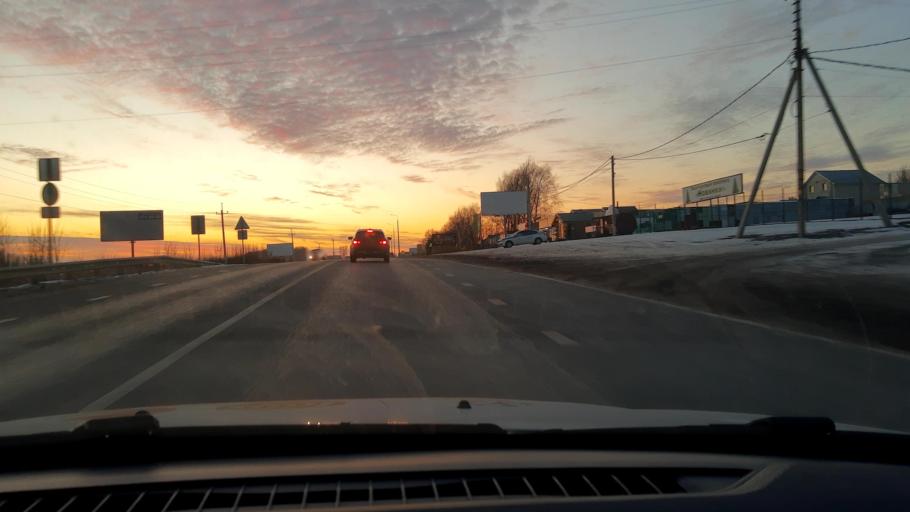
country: RU
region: Nizjnij Novgorod
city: Burevestnik
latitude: 56.2137
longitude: 43.8990
